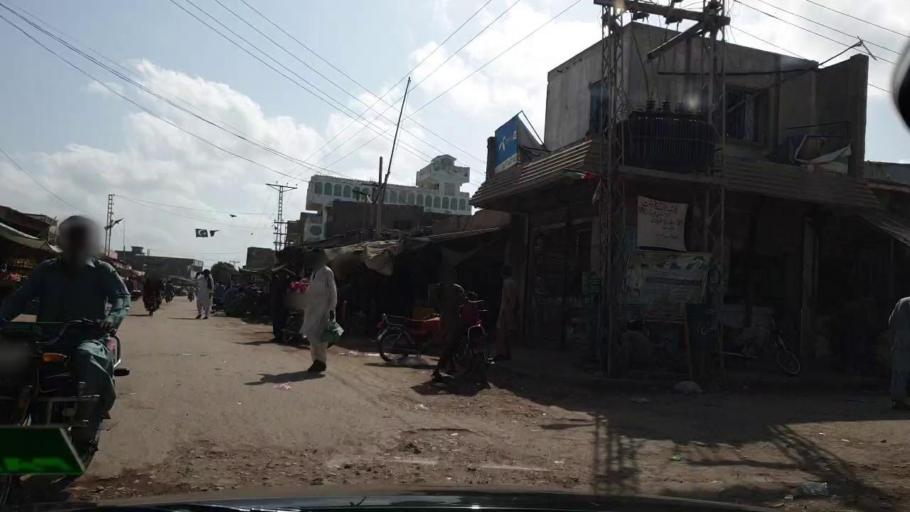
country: PK
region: Sindh
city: Kadhan
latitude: 24.6405
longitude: 69.1156
